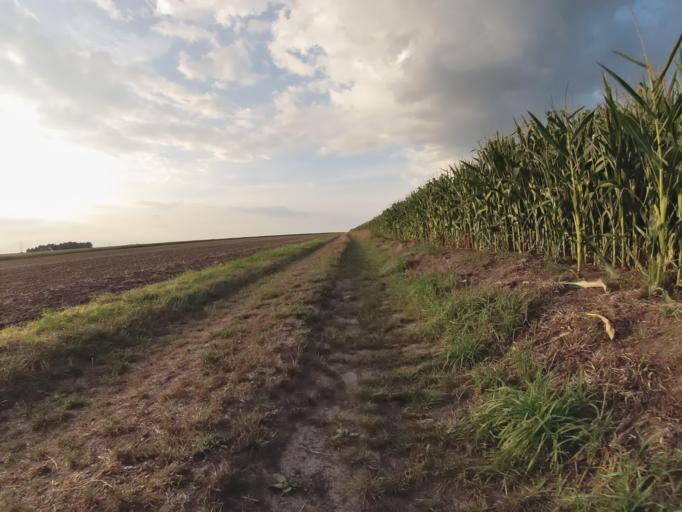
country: DE
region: North Rhine-Westphalia
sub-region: Regierungsbezirk Munster
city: Westerkappeln
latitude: 52.3433
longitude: 7.8890
